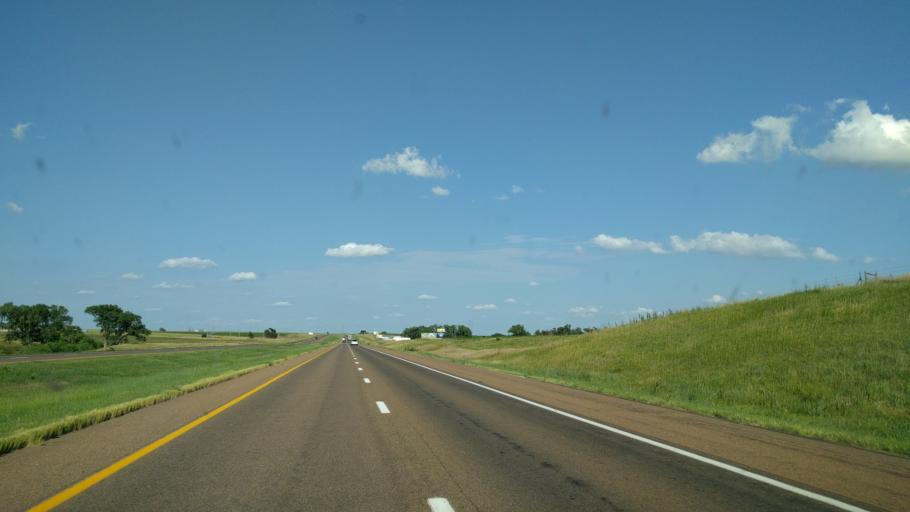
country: US
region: Kansas
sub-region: Ellis County
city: Hays
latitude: 38.9215
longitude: -99.4184
